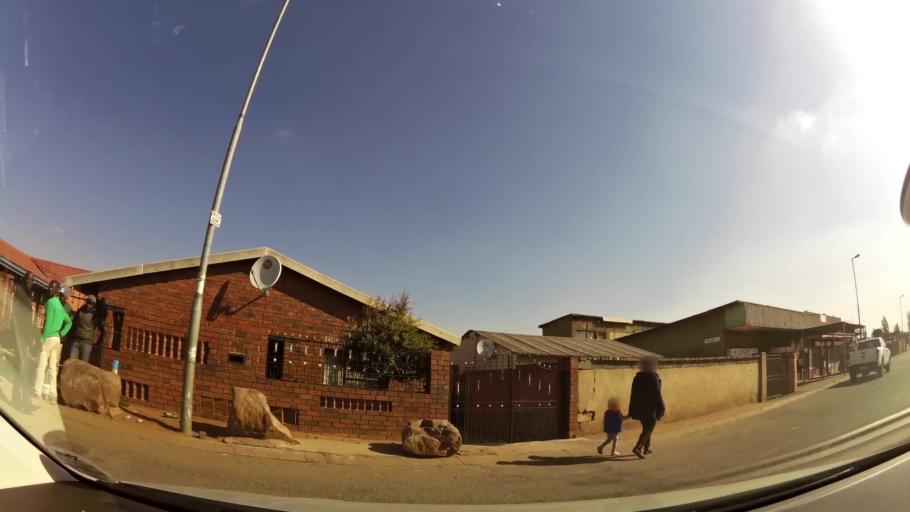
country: ZA
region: Gauteng
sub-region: City of Johannesburg Metropolitan Municipality
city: Soweto
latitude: -26.2835
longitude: 27.8710
